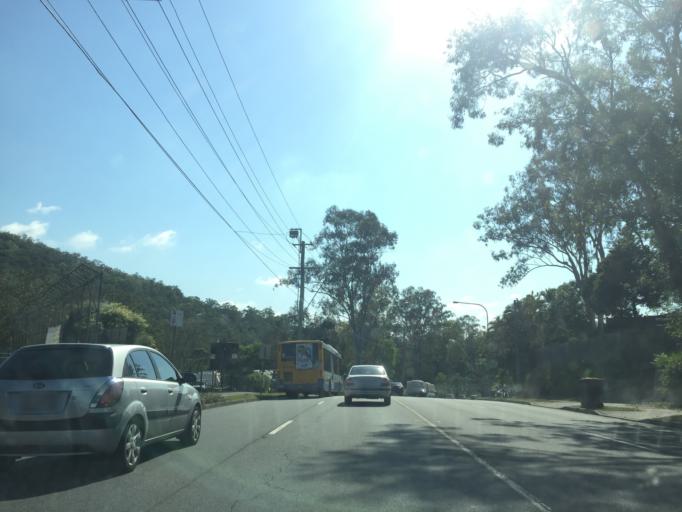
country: AU
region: Queensland
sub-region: Brisbane
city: Toowong
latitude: -27.4464
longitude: 152.9610
